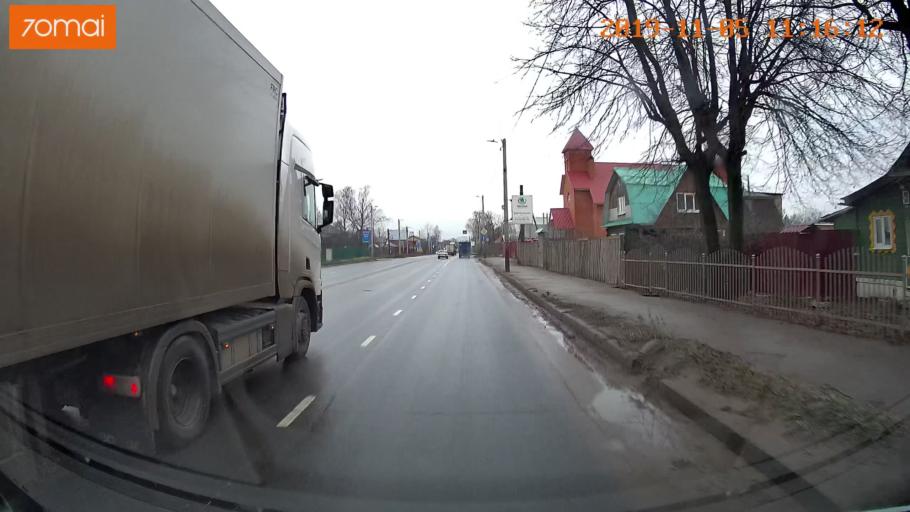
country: RU
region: Ivanovo
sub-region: Gorod Ivanovo
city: Ivanovo
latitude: 56.9828
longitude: 40.9536
